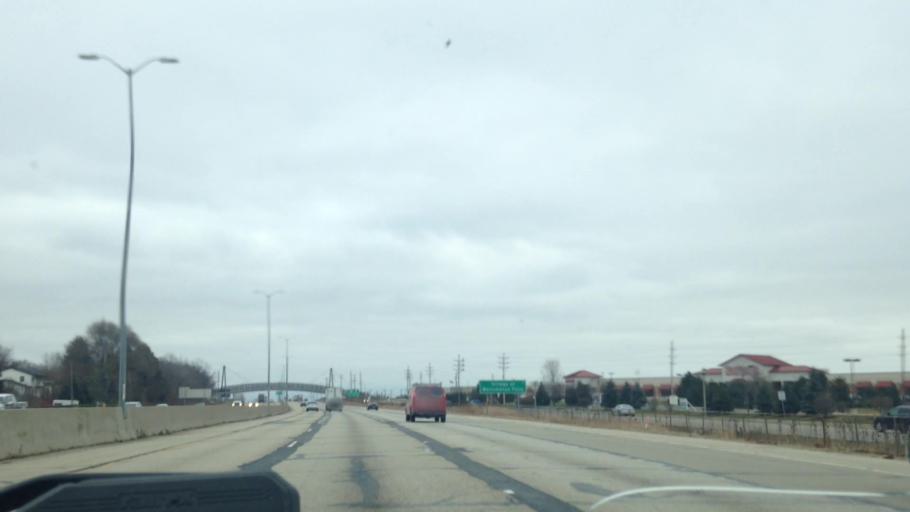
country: US
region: Wisconsin
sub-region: Waukesha County
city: Menomonee Falls
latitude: 43.1901
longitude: -88.1186
